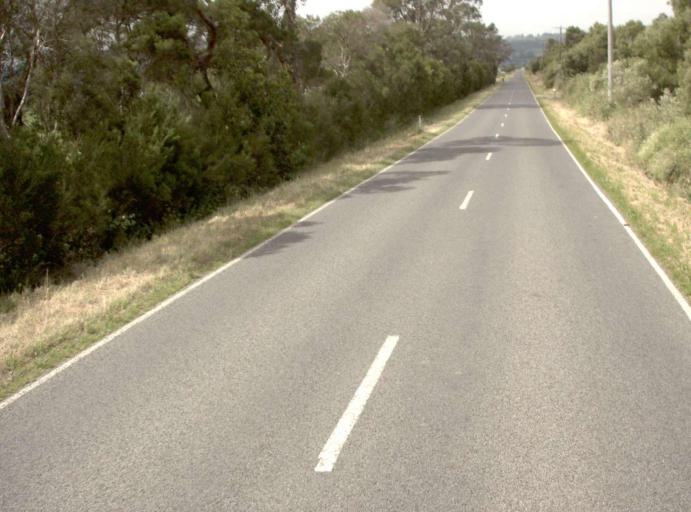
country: AU
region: Victoria
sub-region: Latrobe
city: Moe
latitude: -38.1713
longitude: 146.1445
